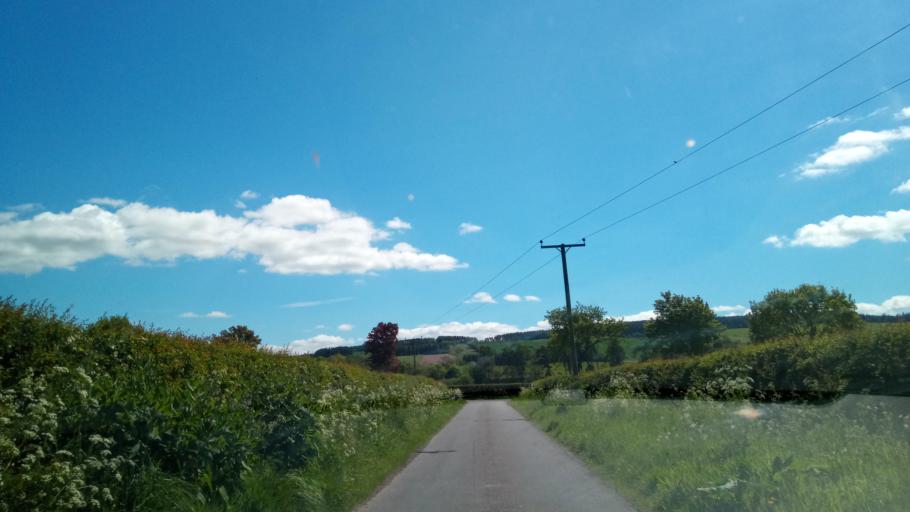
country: GB
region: Scotland
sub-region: The Scottish Borders
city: Saint Boswells
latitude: 55.4684
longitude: -2.6752
